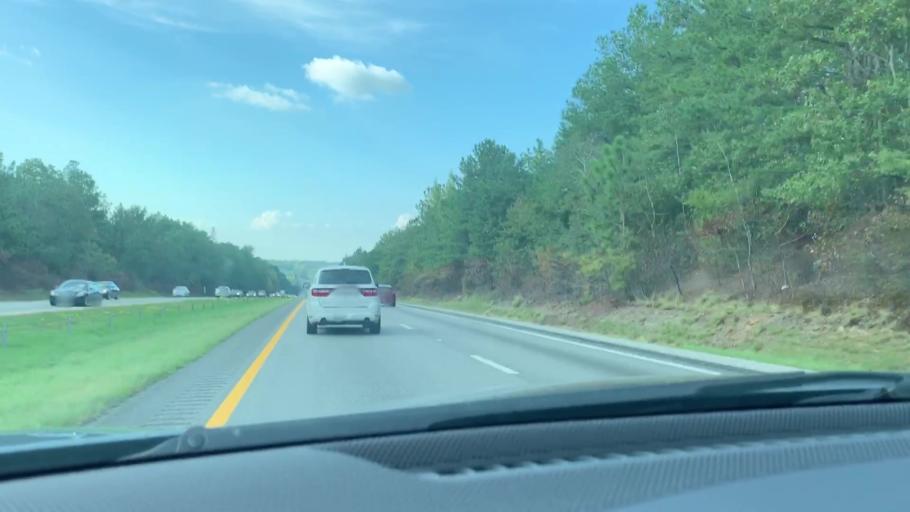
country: US
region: South Carolina
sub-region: Calhoun County
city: Oak Grove
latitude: 33.7409
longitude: -80.9380
